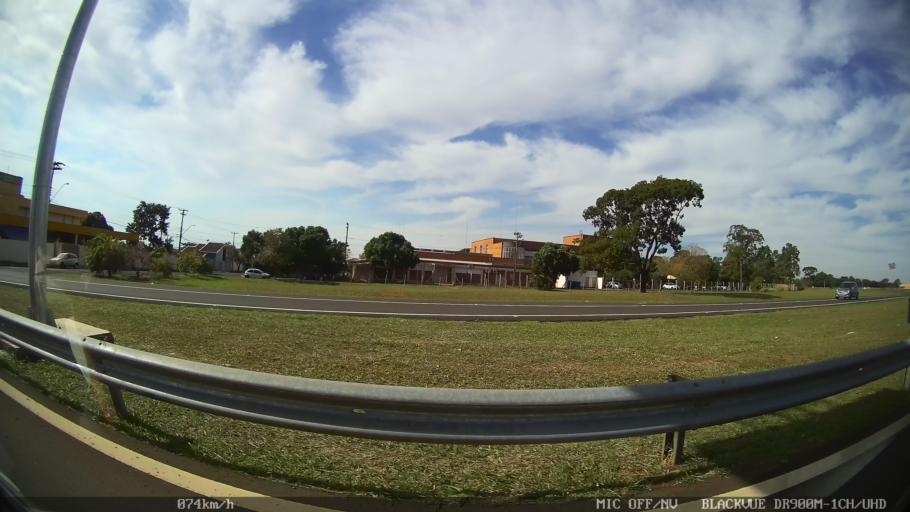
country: BR
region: Sao Paulo
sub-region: Araraquara
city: Araraquara
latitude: -21.8098
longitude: -48.1594
